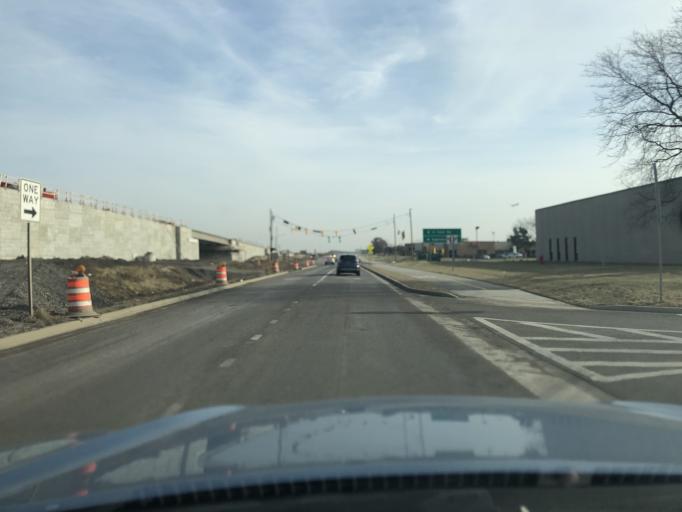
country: US
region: Illinois
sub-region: Cook County
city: Elk Grove Village
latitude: 41.9814
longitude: -87.9543
